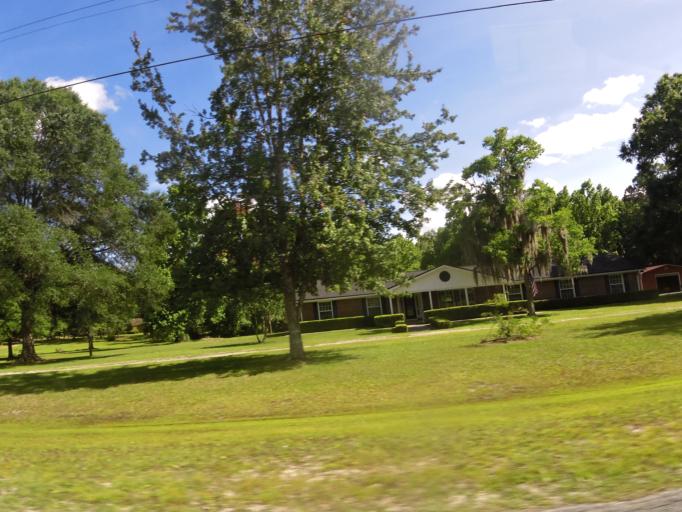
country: US
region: Florida
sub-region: Nassau County
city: Hilliard
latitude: 30.6693
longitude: -81.9181
